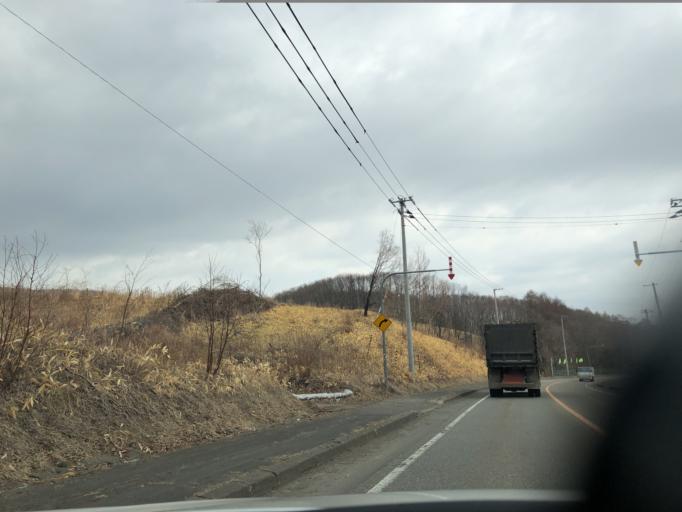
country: JP
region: Hokkaido
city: Chitose
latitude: 42.7627
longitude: 141.8033
